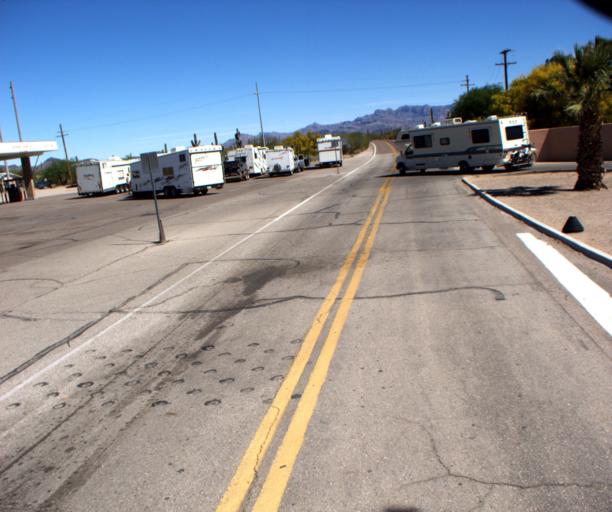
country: MX
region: Sonora
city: Sonoyta
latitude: 31.8810
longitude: -112.8166
